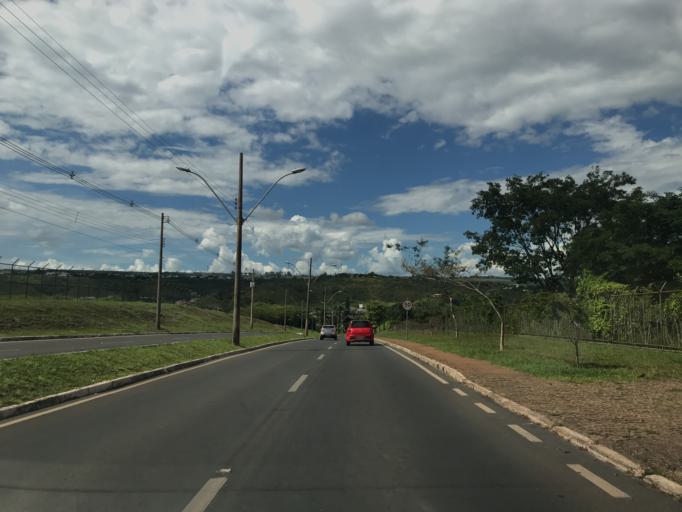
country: BR
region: Federal District
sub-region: Brasilia
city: Brasilia
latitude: -15.7202
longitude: -47.8799
